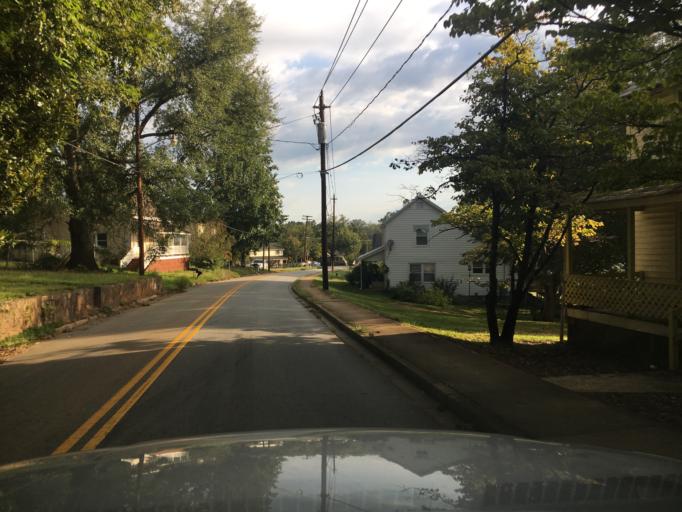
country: US
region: South Carolina
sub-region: Spartanburg County
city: Wellford
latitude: 34.9251
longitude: -82.1034
